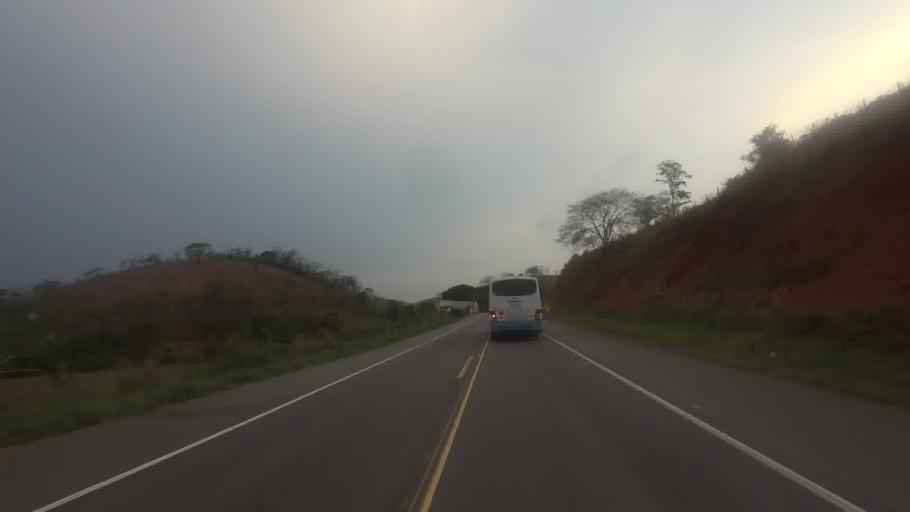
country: BR
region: Rio de Janeiro
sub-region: Carmo
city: Carmo
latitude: -21.8334
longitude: -42.6070
